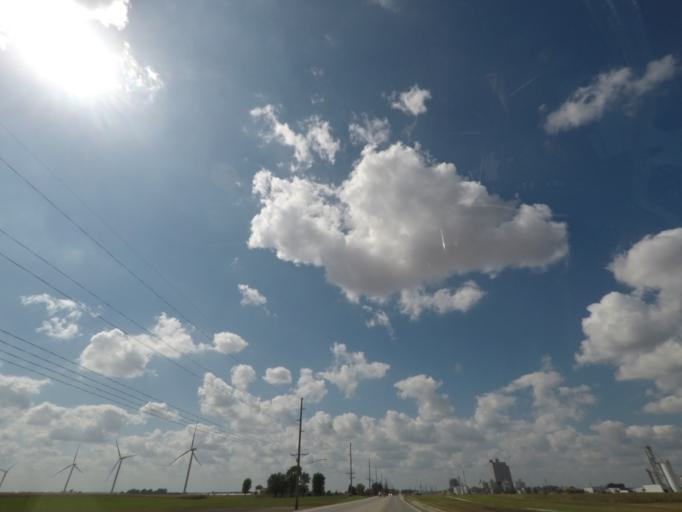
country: US
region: Iowa
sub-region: Story County
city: Nevada
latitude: 42.0231
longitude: -93.5040
